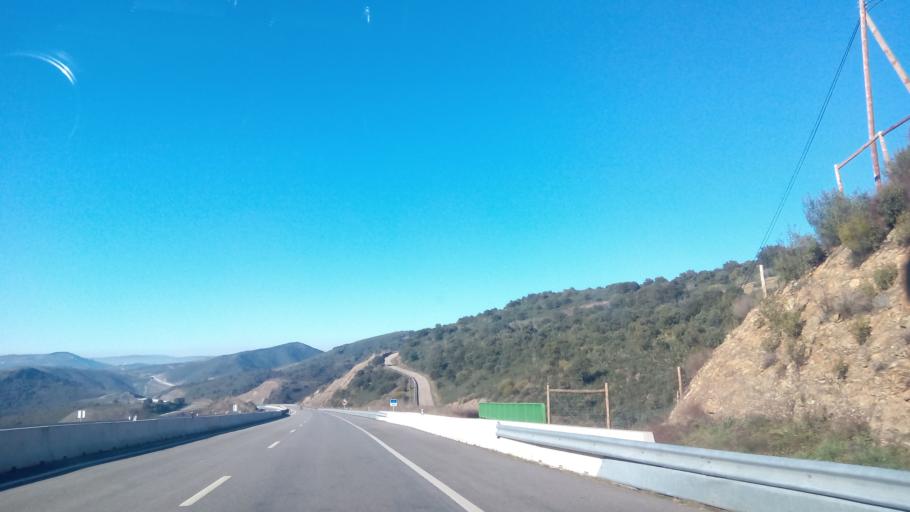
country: PT
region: Braganca
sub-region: Braganca Municipality
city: Braganca
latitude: 41.7635
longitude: -6.6515
